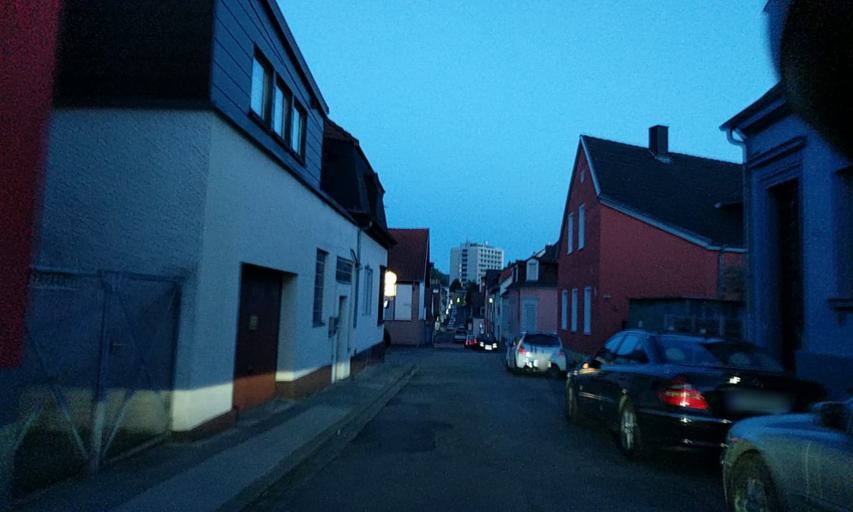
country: DE
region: Rheinland-Pfalz
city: Kaiserslautern
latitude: 49.4445
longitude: 7.7543
